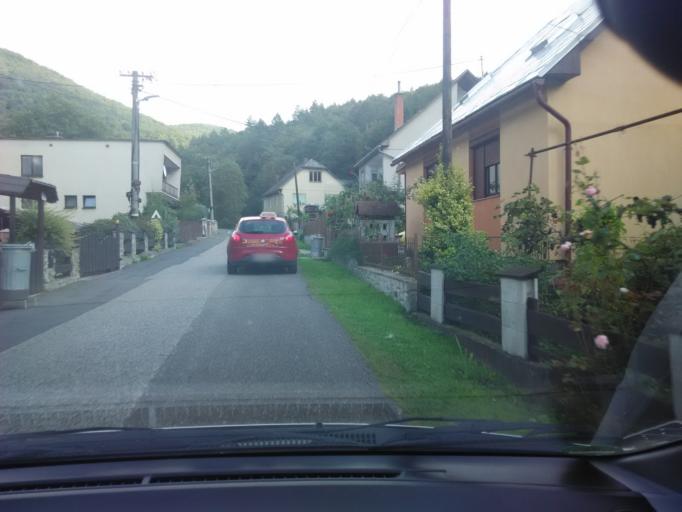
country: SK
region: Banskobystricky
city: Nova Bana
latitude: 48.3965
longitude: 18.6646
